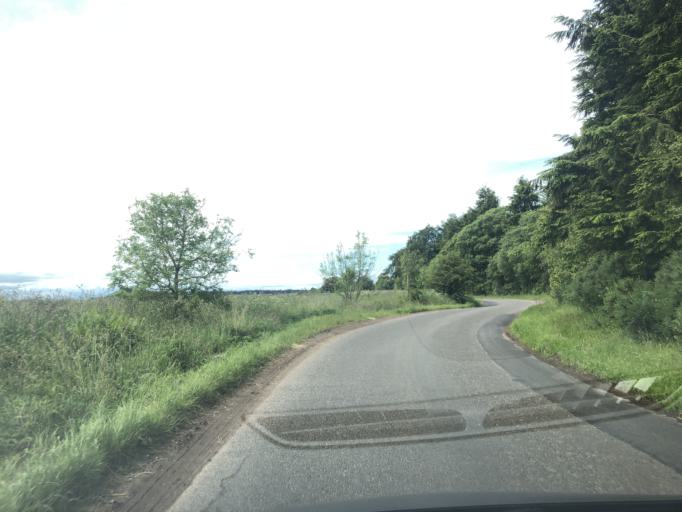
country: GB
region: Scotland
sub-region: Angus
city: Kirriemuir
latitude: 56.6962
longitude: -2.9494
